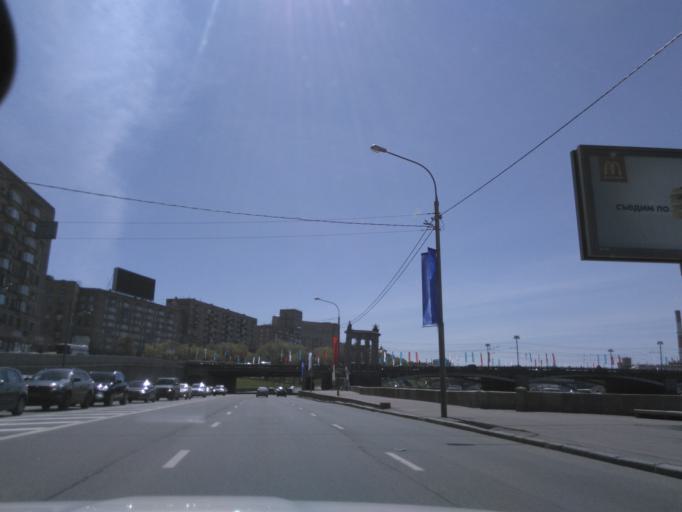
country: RU
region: Moskovskaya
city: Dorogomilovo
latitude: 55.7471
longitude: 37.5760
